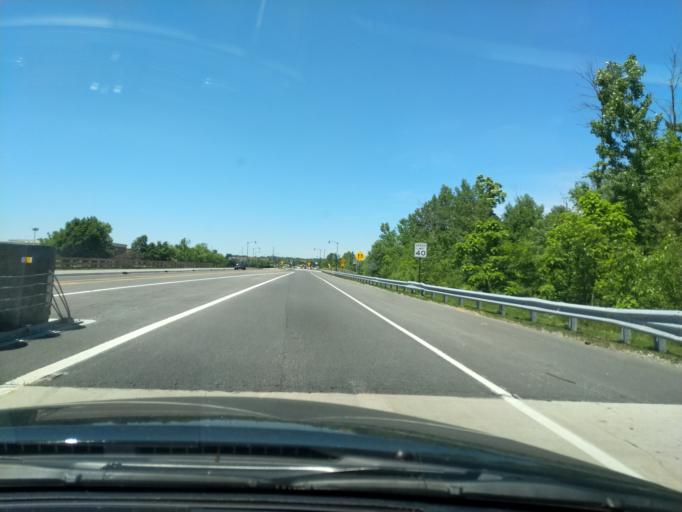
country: US
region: Indiana
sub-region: Hamilton County
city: Carmel
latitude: 39.9955
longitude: -86.1226
